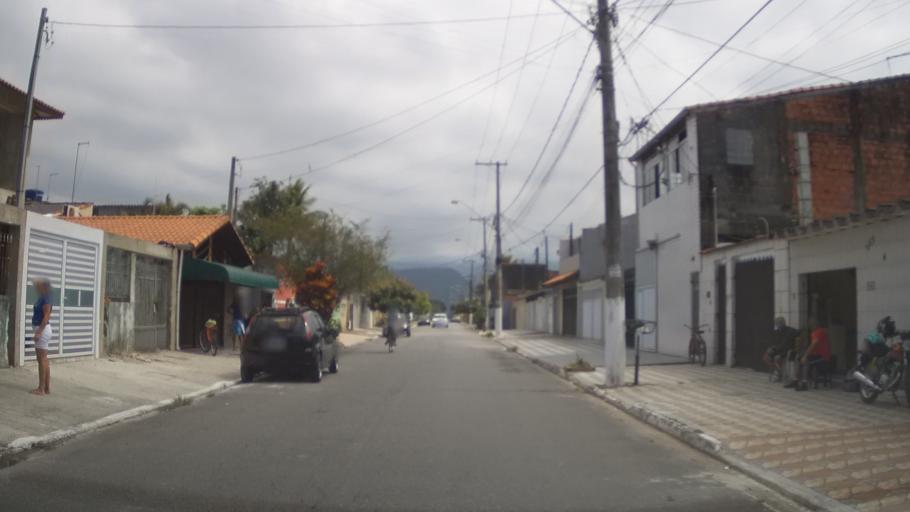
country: BR
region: Sao Paulo
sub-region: Praia Grande
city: Praia Grande
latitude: -24.0236
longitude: -46.4950
